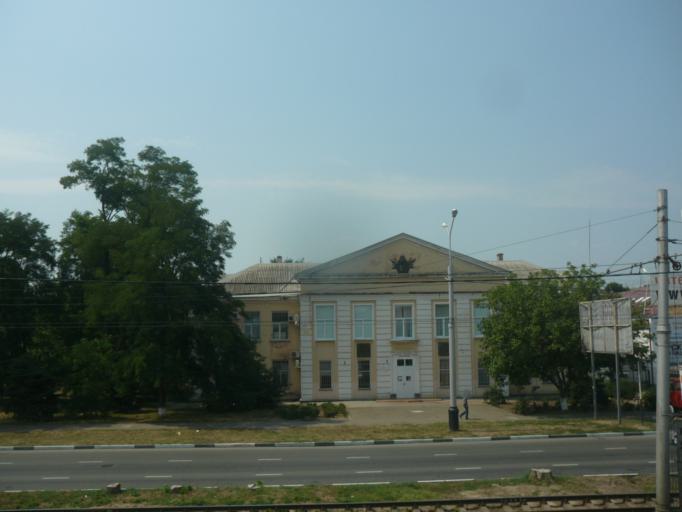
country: RU
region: Adygeya
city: Yablonovskiy
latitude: 45.0024
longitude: 38.9648
